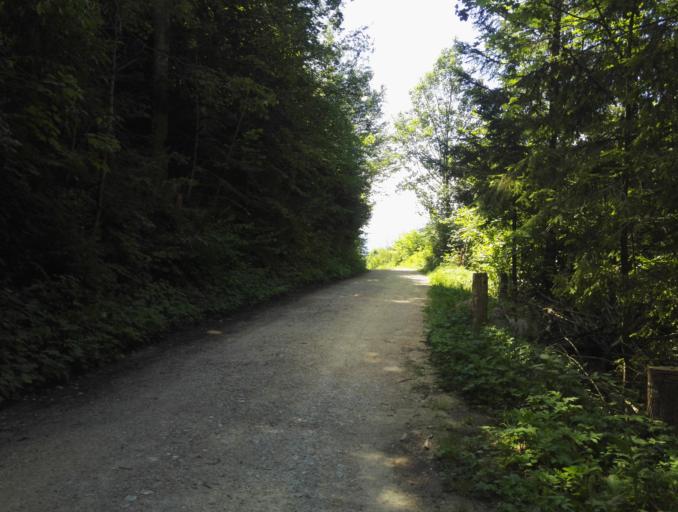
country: AT
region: Styria
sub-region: Politischer Bezirk Graz-Umgebung
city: Rothelstein
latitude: 47.3420
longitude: 15.3920
